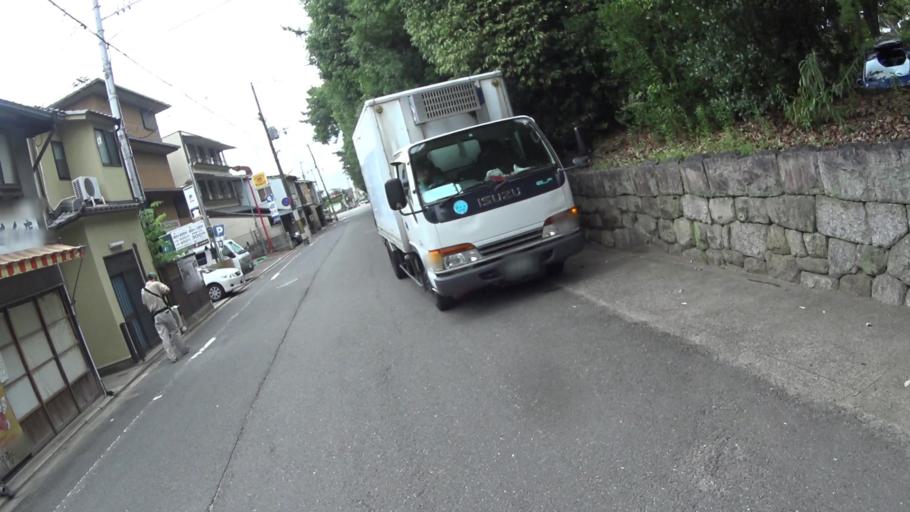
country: JP
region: Kyoto
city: Kyoto
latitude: 35.0291
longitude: 135.7362
